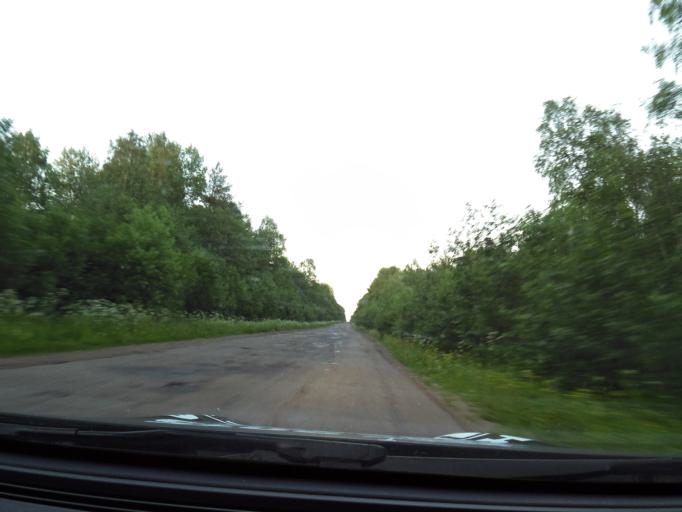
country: RU
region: Leningrad
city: Voznesen'ye
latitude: 60.8470
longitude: 35.6030
